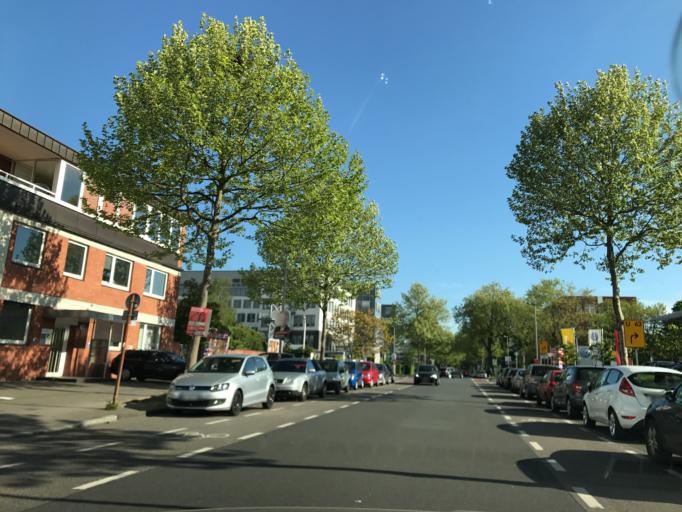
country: DE
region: North Rhine-Westphalia
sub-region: Regierungsbezirk Dusseldorf
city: Neuss
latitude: 51.2378
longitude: 6.7207
